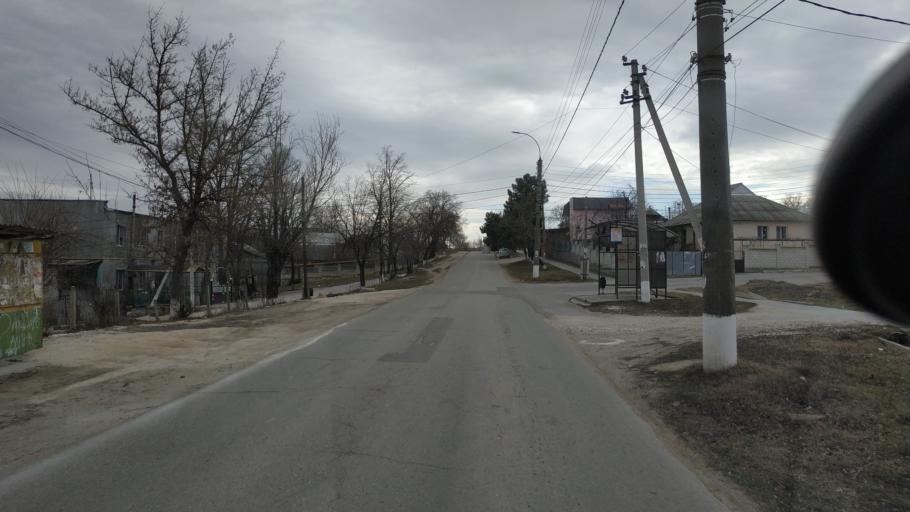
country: MD
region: Chisinau
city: Vadul lui Voda
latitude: 47.0967
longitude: 29.0709
